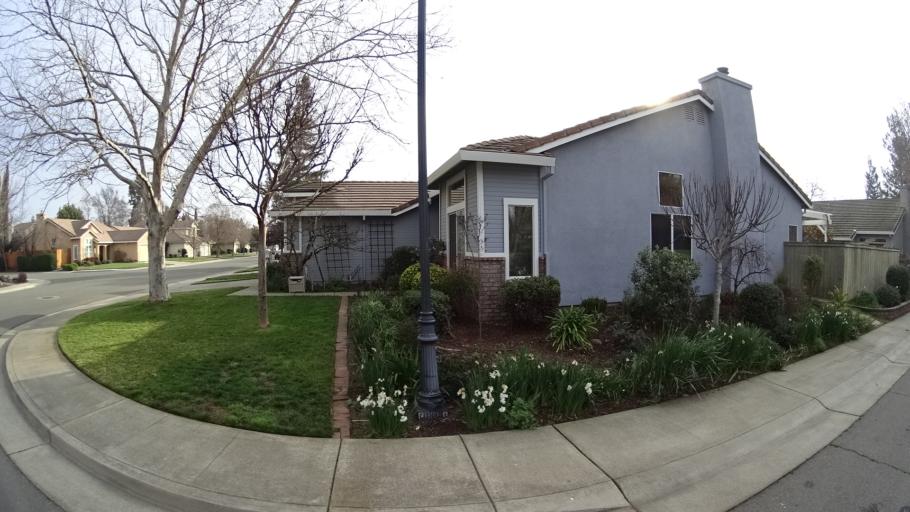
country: US
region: California
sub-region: Yolo County
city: Davis
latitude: 38.5597
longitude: -121.7122
